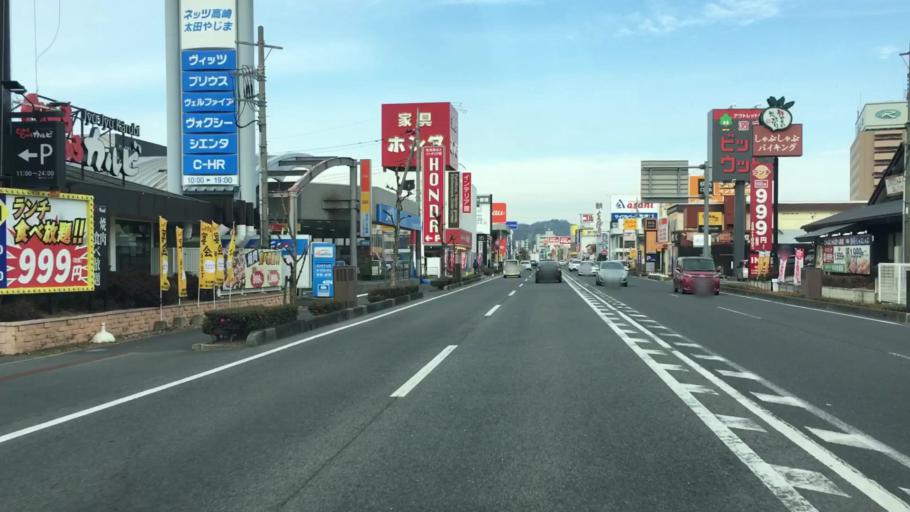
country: JP
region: Gunma
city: Ota
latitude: 36.2771
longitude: 139.3772
